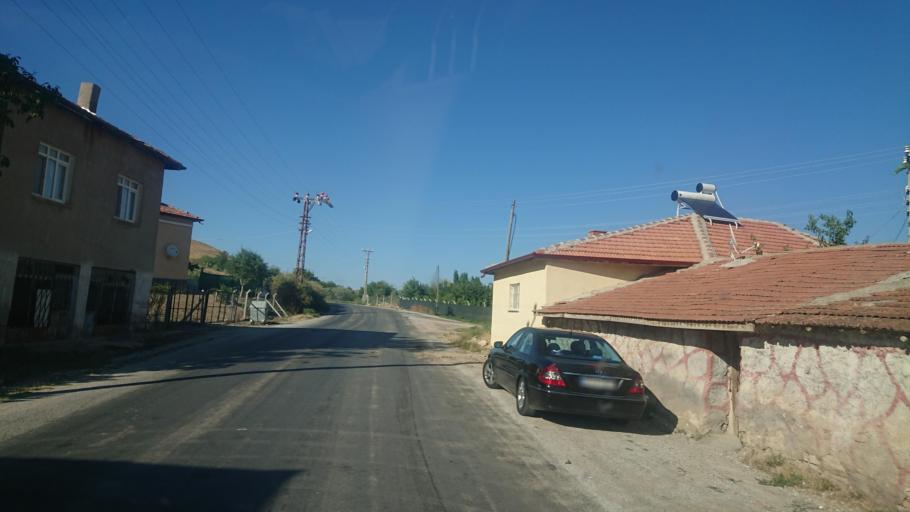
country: TR
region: Ankara
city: Sereflikochisar
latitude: 38.7676
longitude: 33.7014
